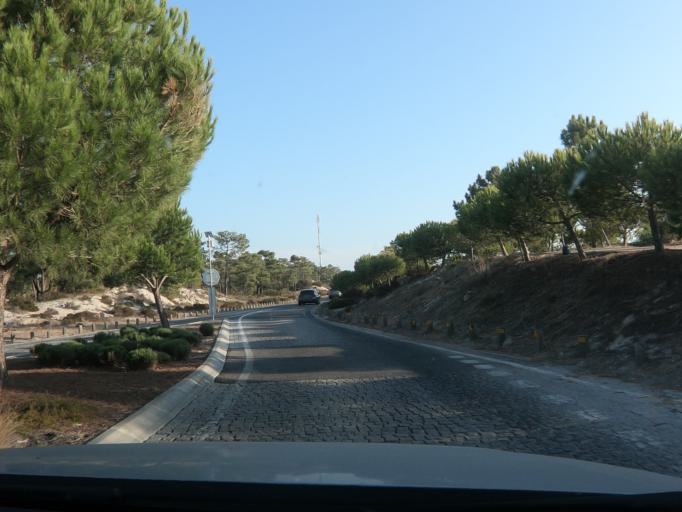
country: PT
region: Setubal
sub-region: Setubal
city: Setubal
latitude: 38.4732
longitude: -8.8850
